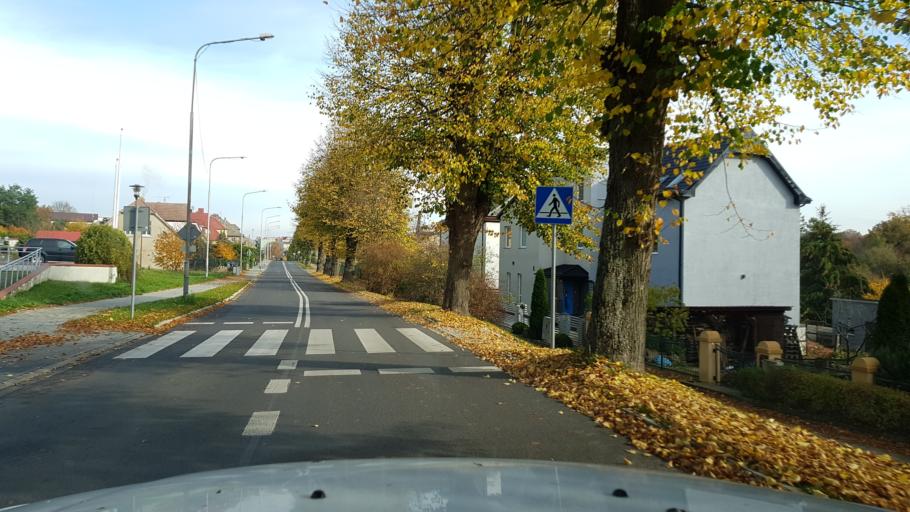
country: PL
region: West Pomeranian Voivodeship
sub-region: Powiat swidwinski
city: Polczyn-Zdroj
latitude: 53.7625
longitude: 16.0860
